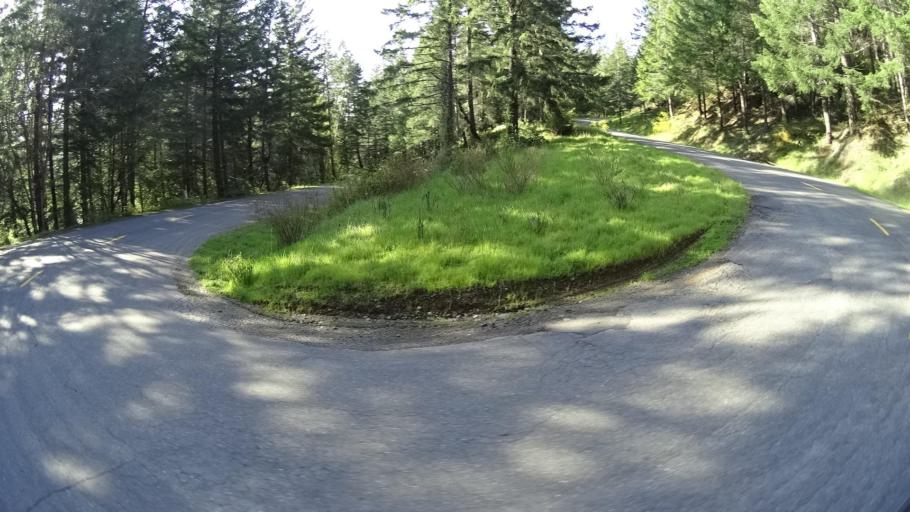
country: US
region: California
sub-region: Humboldt County
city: Rio Dell
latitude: 40.3283
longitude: -124.0438
